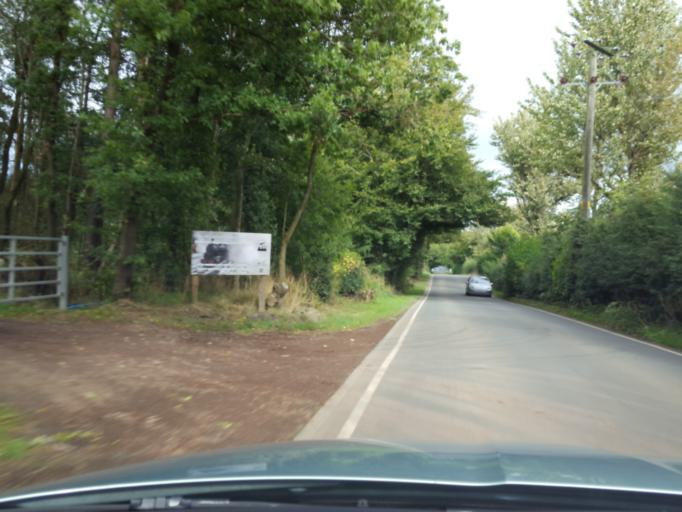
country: GB
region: Scotland
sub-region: West Lothian
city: Broxburn
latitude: 55.9161
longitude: -3.4657
